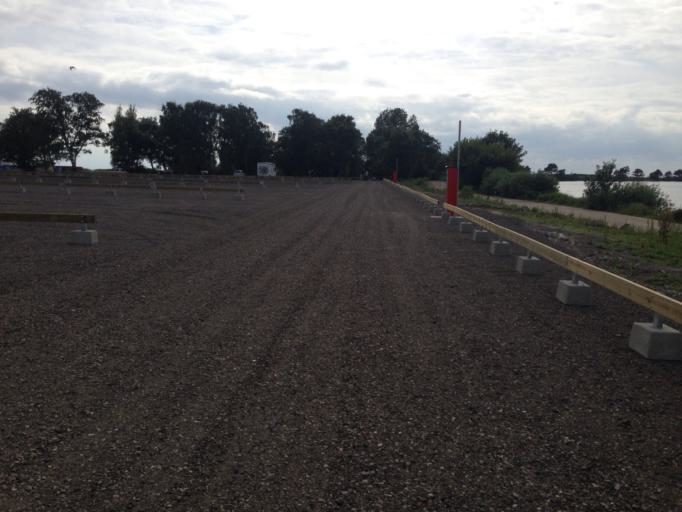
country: SE
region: Skane
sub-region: Lomma Kommun
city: Lomma
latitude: 55.6836
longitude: 13.0643
